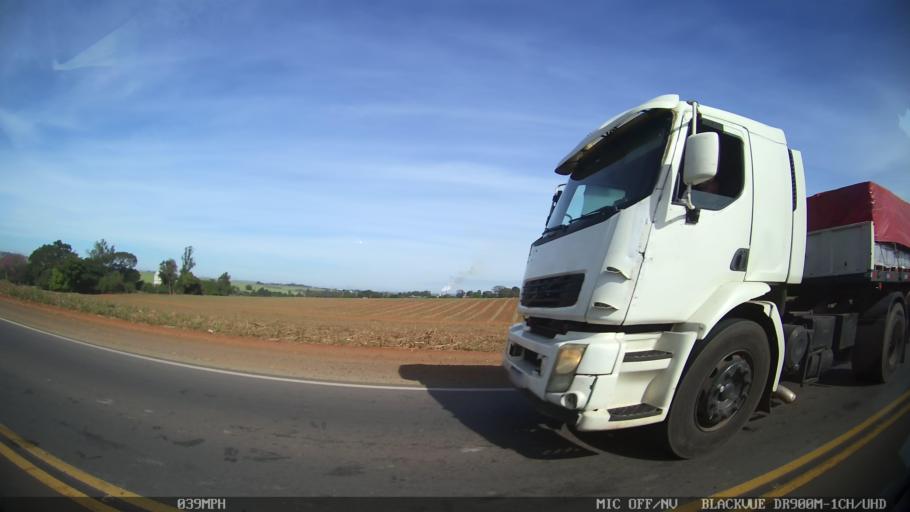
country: BR
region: Sao Paulo
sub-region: Piracicaba
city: Piracicaba
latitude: -22.7891
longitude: -47.6465
